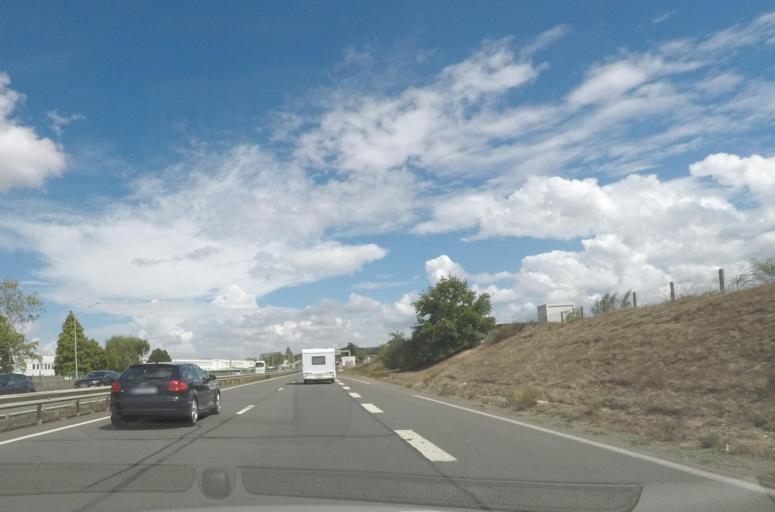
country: FR
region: Pays de la Loire
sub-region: Departement de la Sarthe
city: Arnage
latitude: 47.9457
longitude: 0.1935
